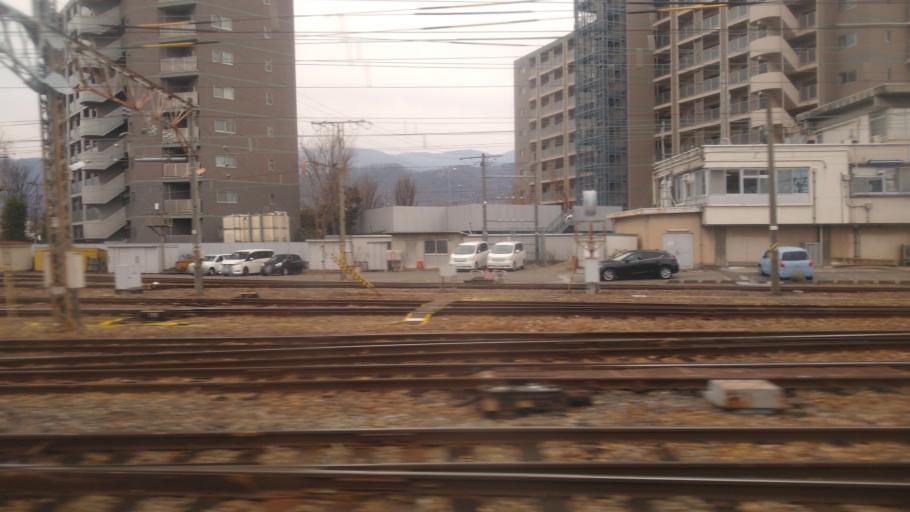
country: JP
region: Nagano
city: Matsumoto
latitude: 36.2081
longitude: 137.9688
